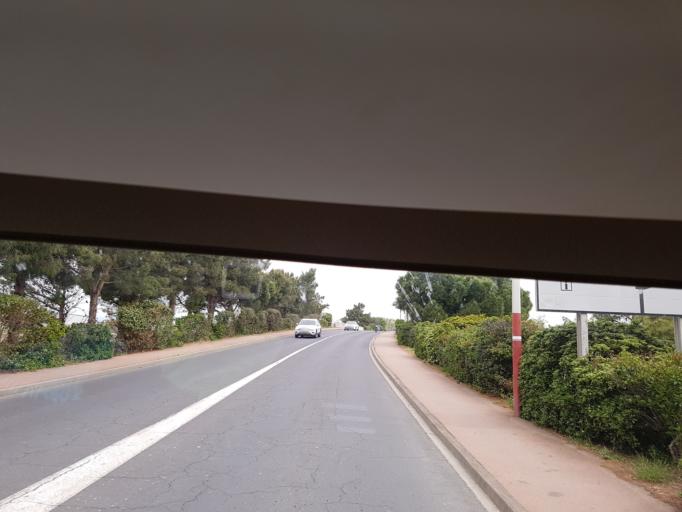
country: FR
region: Languedoc-Roussillon
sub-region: Departement de l'Aude
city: Narbonne
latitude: 43.1712
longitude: 2.9902
